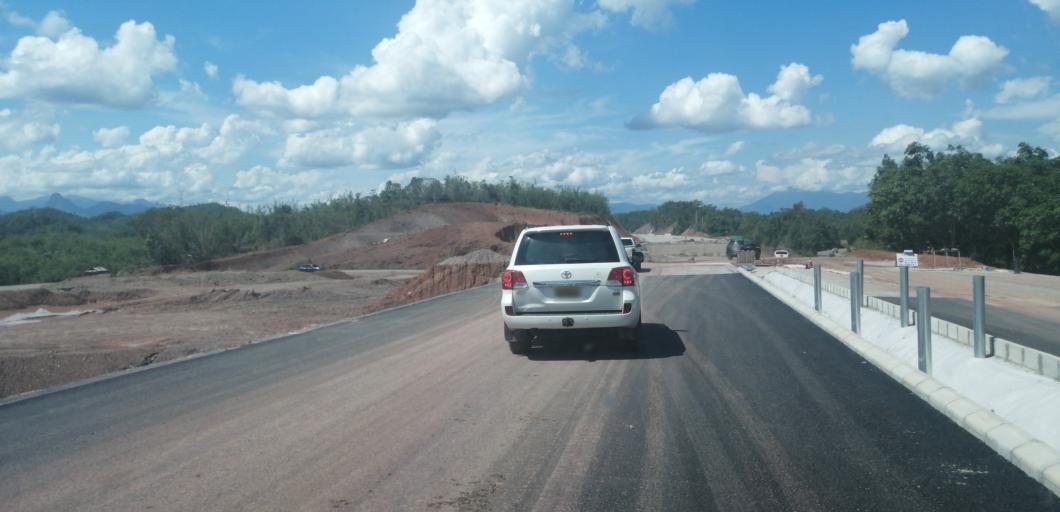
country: LA
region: Vientiane
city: Vangviang
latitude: 18.7295
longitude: 102.3722
